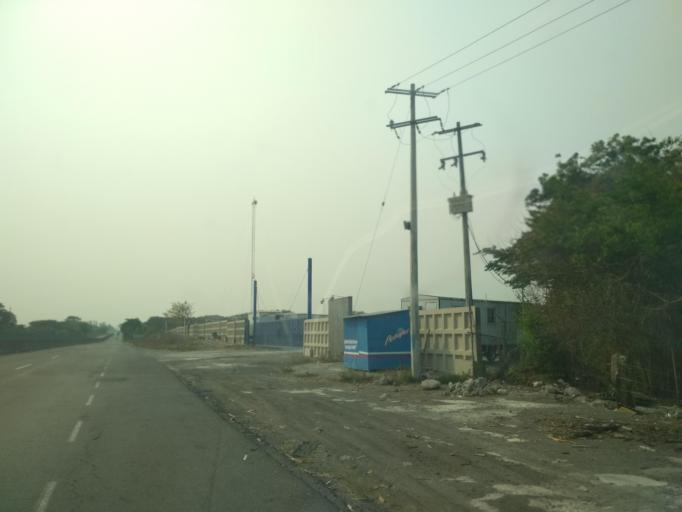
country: MX
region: Veracruz
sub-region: Veracruz
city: Las Amapolas
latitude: 19.1299
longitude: -96.2464
